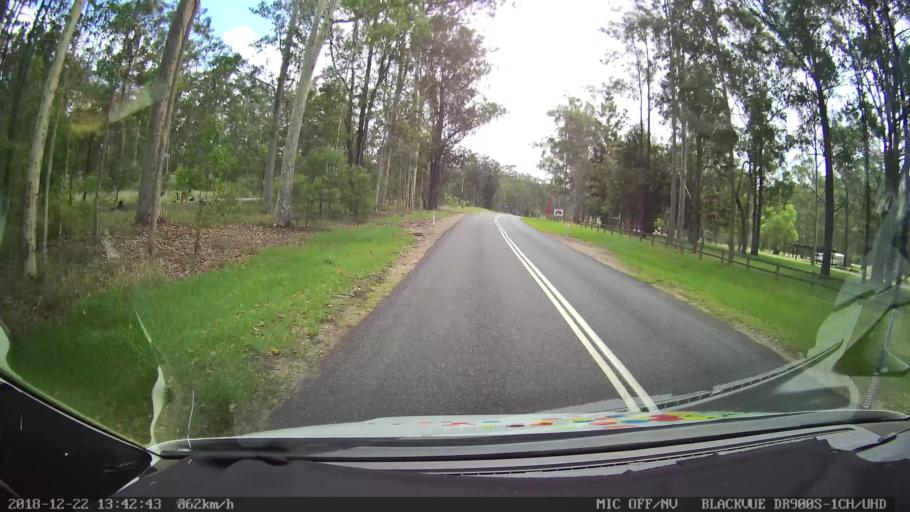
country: AU
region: New South Wales
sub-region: Clarence Valley
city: Coutts Crossing
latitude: -29.9250
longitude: 152.7506
